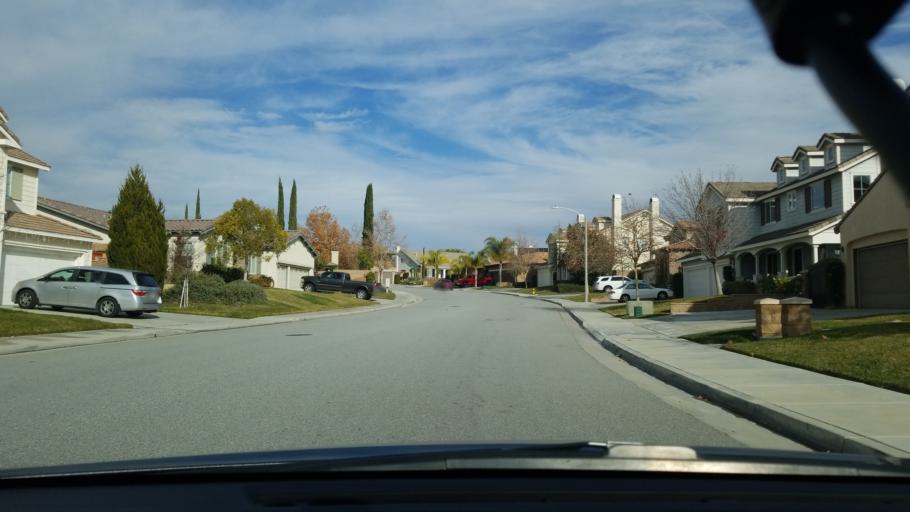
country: US
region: California
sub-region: Riverside County
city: Temecula
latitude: 33.4668
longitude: -117.0666
